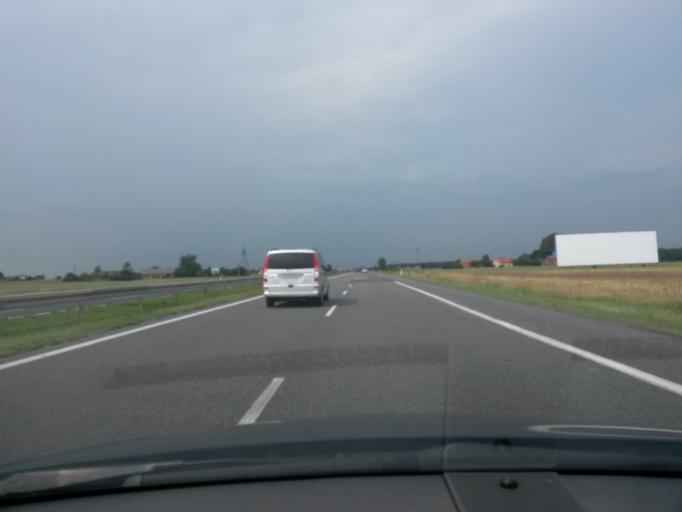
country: PL
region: Lodz Voivodeship
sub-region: Powiat piotrkowski
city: Wola Krzysztoporska
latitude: 51.3736
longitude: 19.6194
